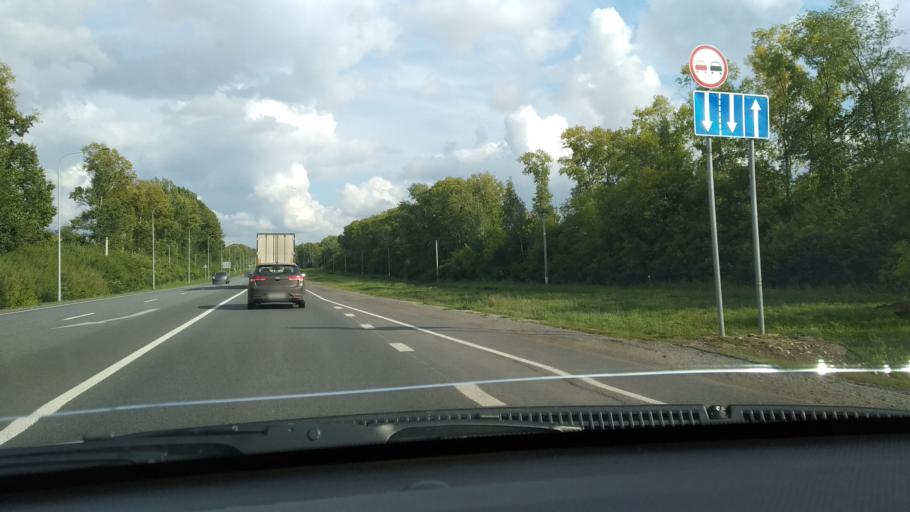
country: RU
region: Tatarstan
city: Stolbishchi
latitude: 55.6549
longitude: 49.3142
